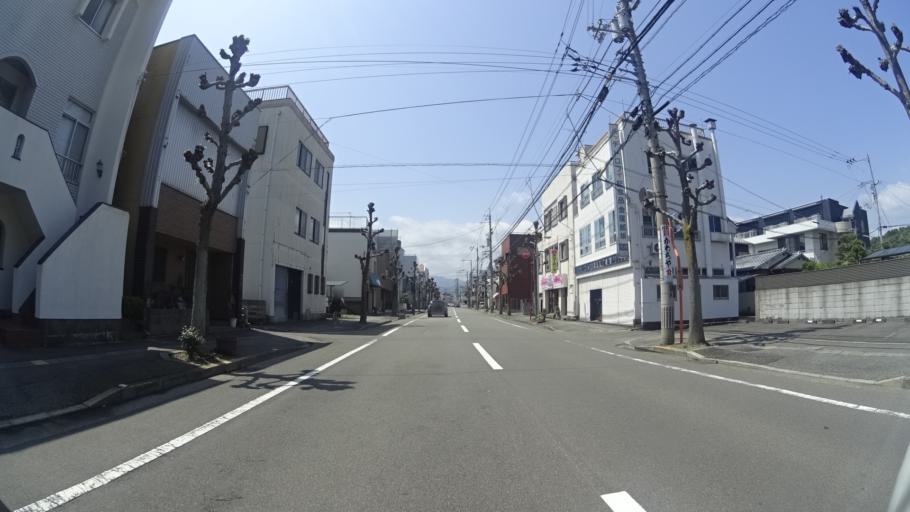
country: JP
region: Tokushima
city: Tokushima-shi
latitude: 34.0617
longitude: 134.5520
